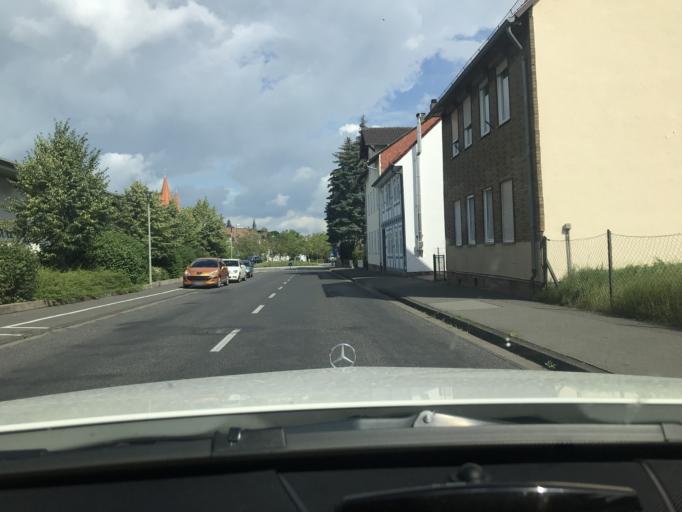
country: DE
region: Hesse
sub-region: Regierungsbezirk Kassel
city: Eschwege
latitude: 51.1845
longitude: 10.0648
